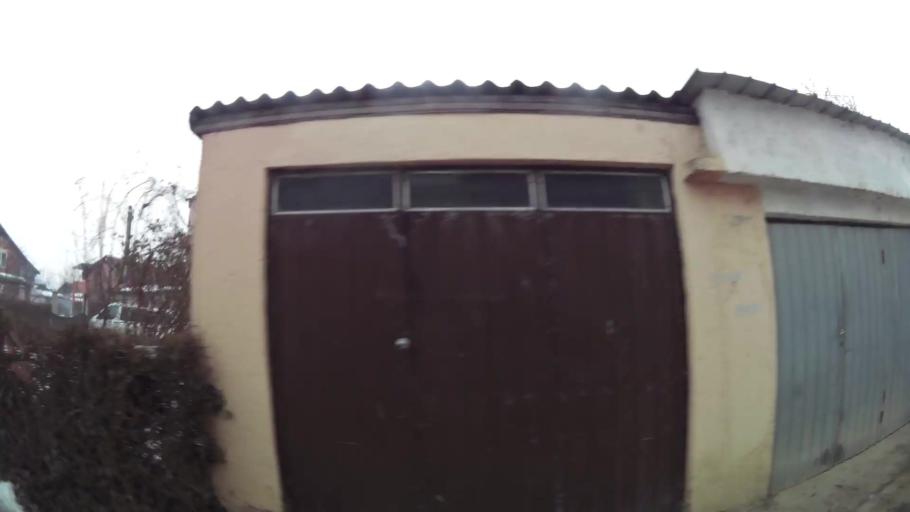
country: MK
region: Saraj
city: Saraj
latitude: 42.0350
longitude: 21.3529
